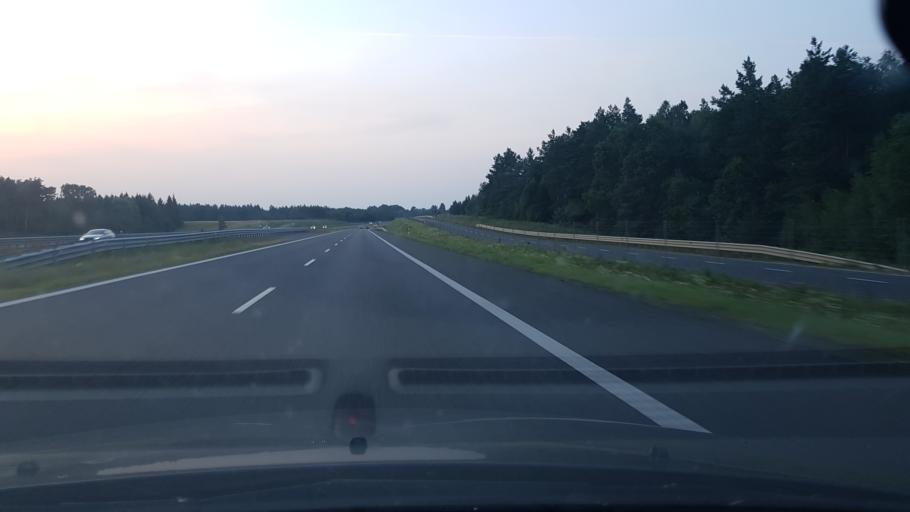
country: PL
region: Warmian-Masurian Voivodeship
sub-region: Powiat olsztynski
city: Olsztynek
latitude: 53.4666
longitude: 20.3220
